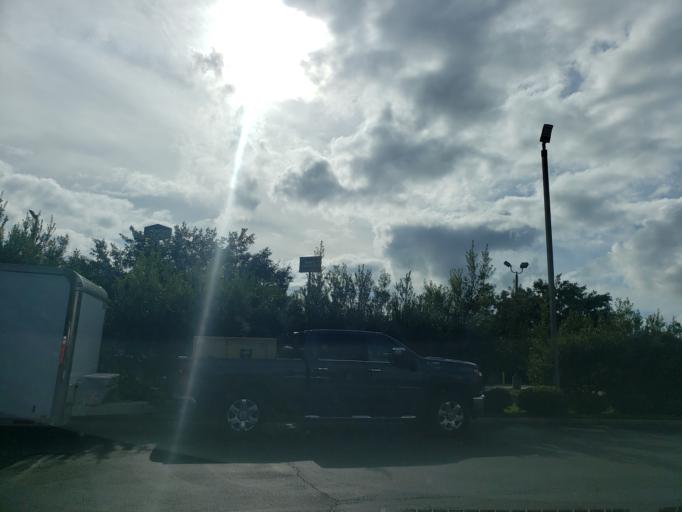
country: US
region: Georgia
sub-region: Chatham County
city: Georgetown
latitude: 32.0080
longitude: -81.2763
